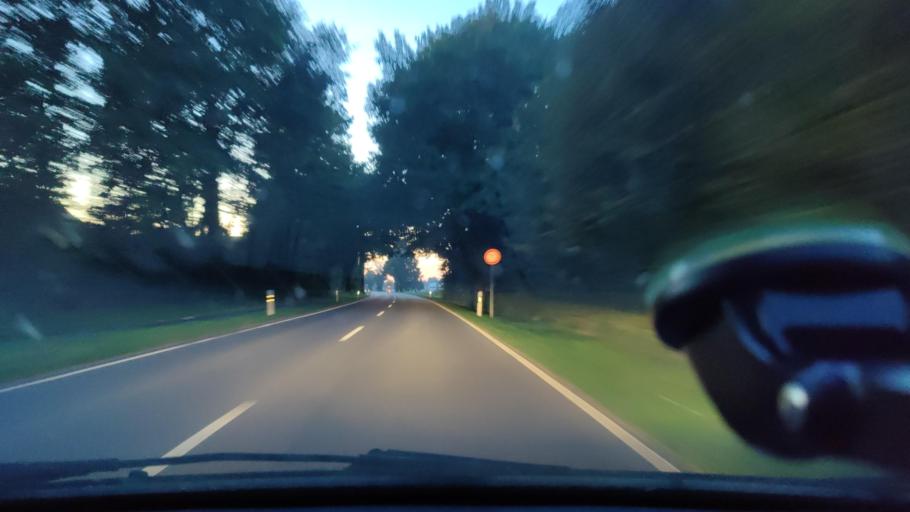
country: DE
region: North Rhine-Westphalia
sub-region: Regierungsbezirk Munster
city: Sudlohn
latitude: 51.9017
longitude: 6.8718
